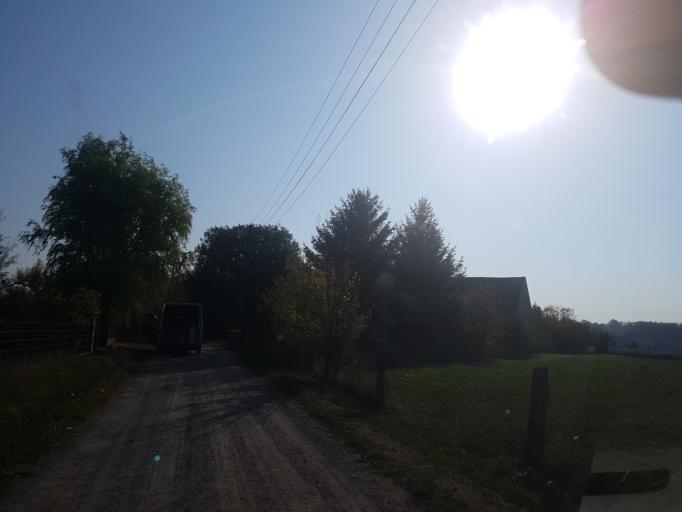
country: DE
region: Brandenburg
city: Finsterwalde
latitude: 51.6102
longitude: 13.7230
